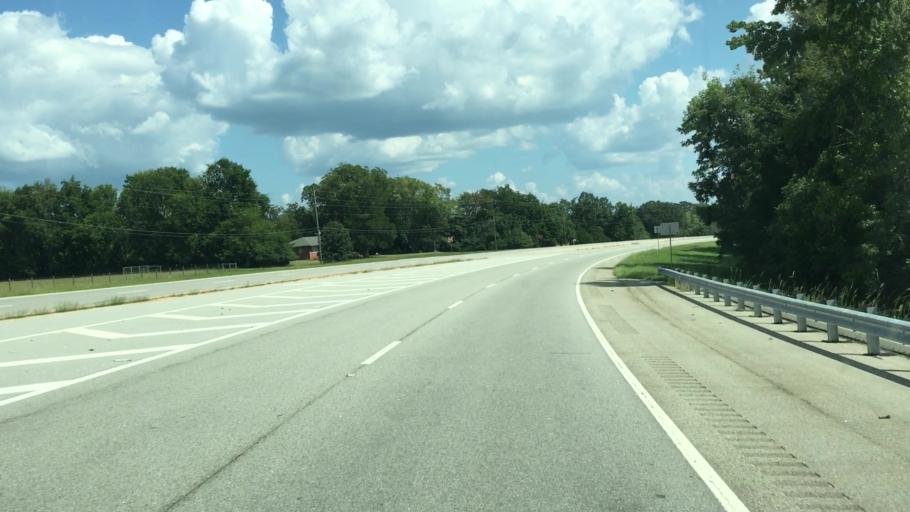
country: US
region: Georgia
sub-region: Putnam County
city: Eatonton
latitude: 33.2687
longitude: -83.3374
